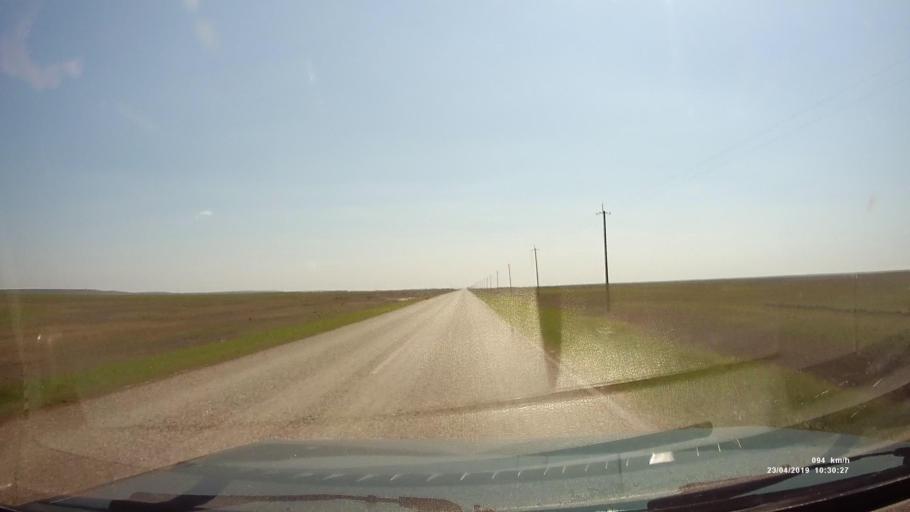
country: RU
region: Kalmykiya
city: Yashalta
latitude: 46.5921
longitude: 42.5447
